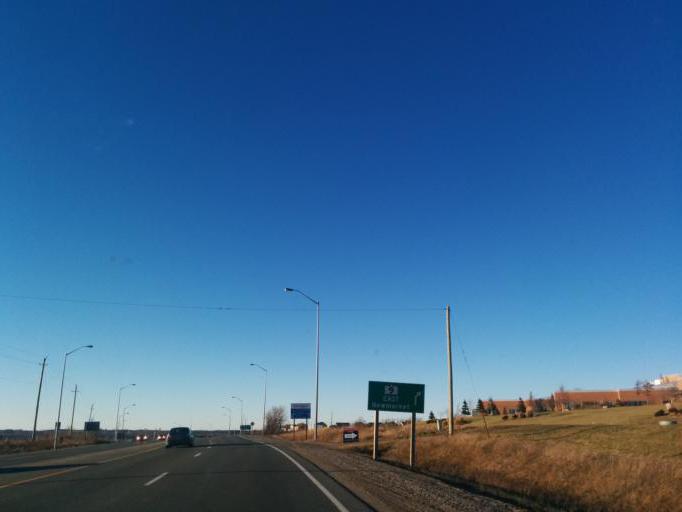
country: CA
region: Ontario
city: Orangeville
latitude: 43.9176
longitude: -80.0740
